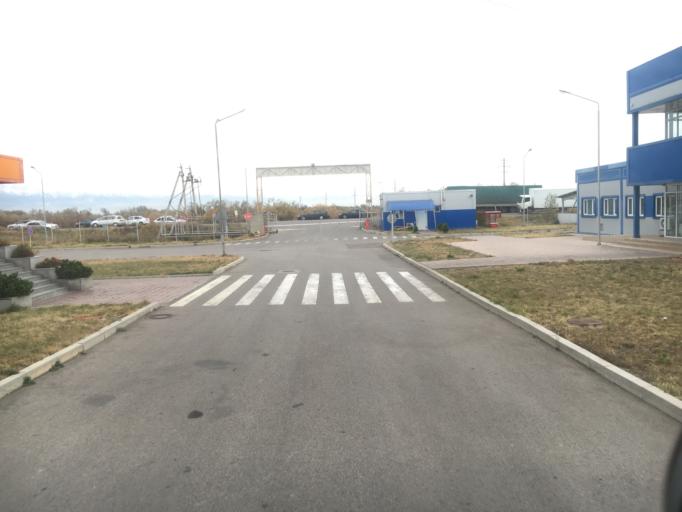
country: KZ
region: Almaty Oblysy
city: Energeticheskiy
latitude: 43.5842
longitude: 77.0929
